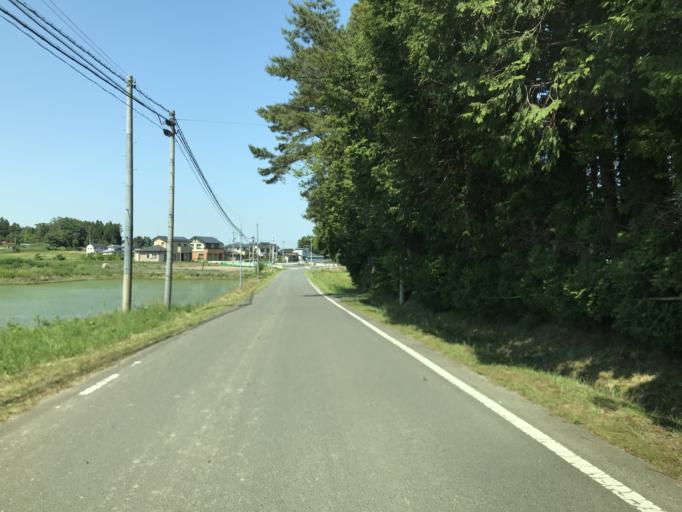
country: JP
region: Miyagi
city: Marumori
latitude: 37.8634
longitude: 140.9097
